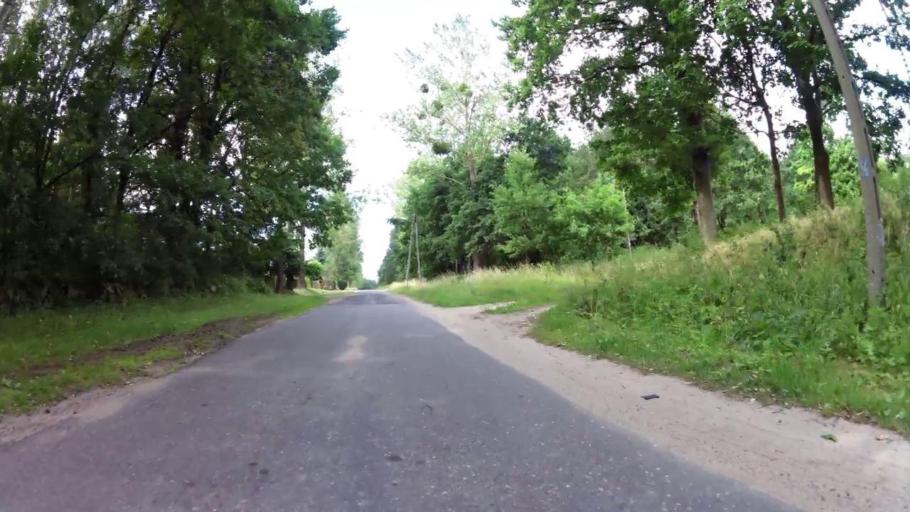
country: PL
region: West Pomeranian Voivodeship
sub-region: Powiat lobeski
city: Lobez
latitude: 53.6031
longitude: 15.6611
